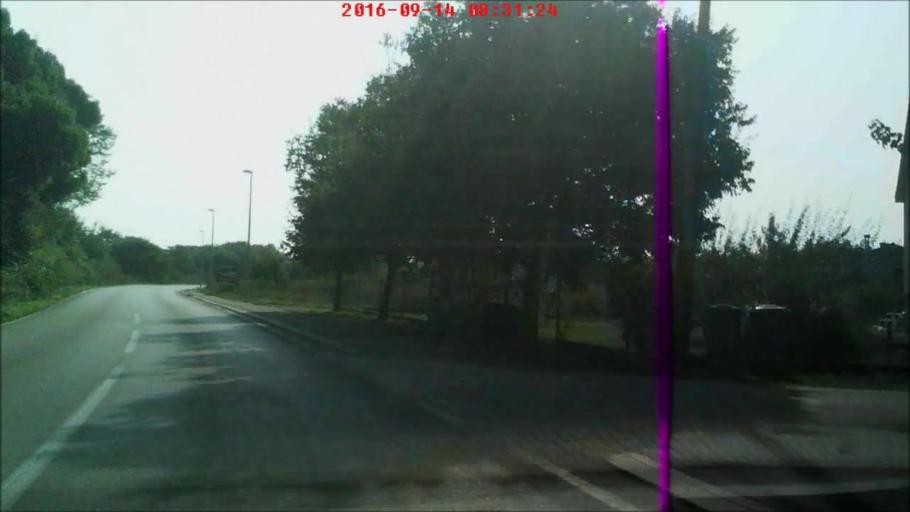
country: HR
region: Zadarska
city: Zadar
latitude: 44.1671
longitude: 15.2966
